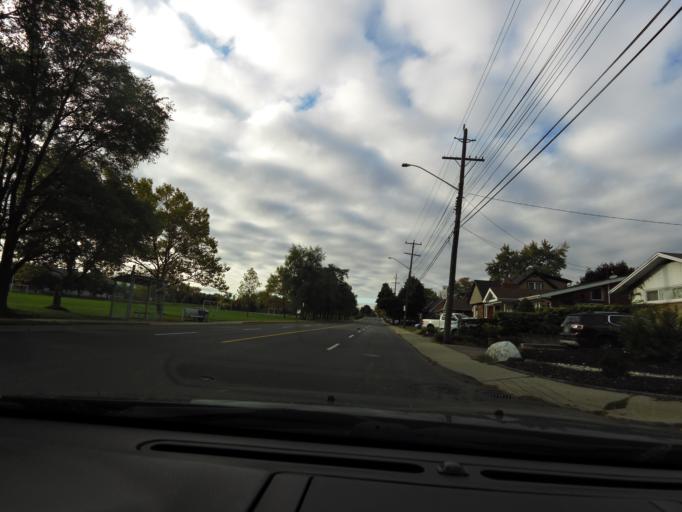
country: CA
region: Ontario
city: Hamilton
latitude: 43.2413
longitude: -79.8973
